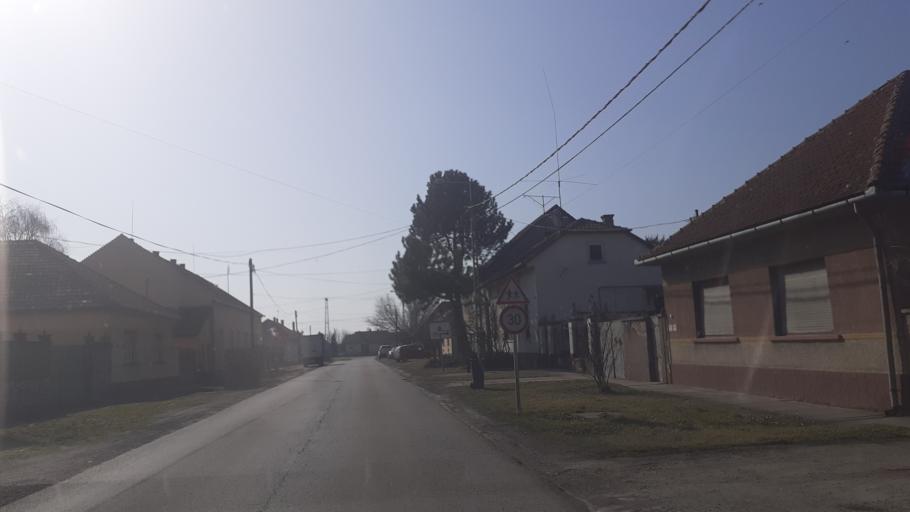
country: HU
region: Bacs-Kiskun
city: Lajosmizse
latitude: 47.0295
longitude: 19.5451
